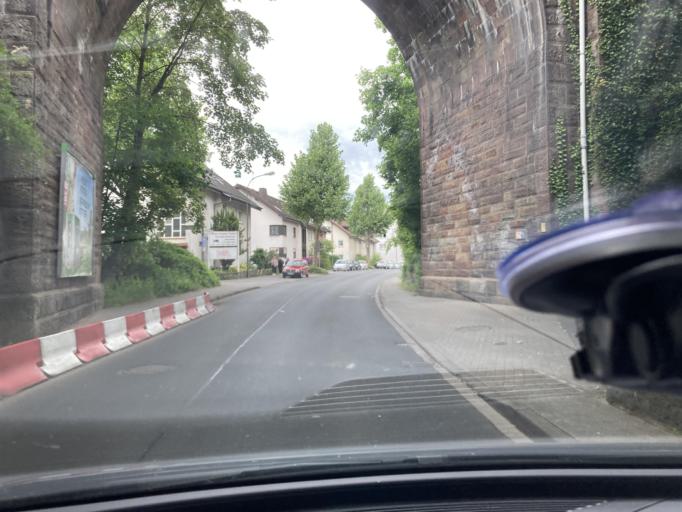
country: DE
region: Hesse
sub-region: Regierungsbezirk Kassel
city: Fulda
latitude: 50.5622
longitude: 9.6621
